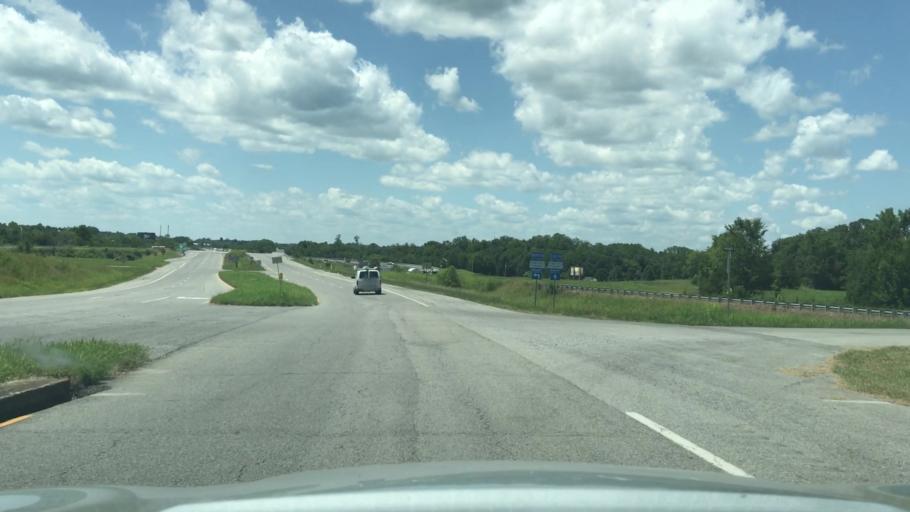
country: US
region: Kentucky
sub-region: Christian County
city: Hopkinsville
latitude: 36.8935
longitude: -87.4651
